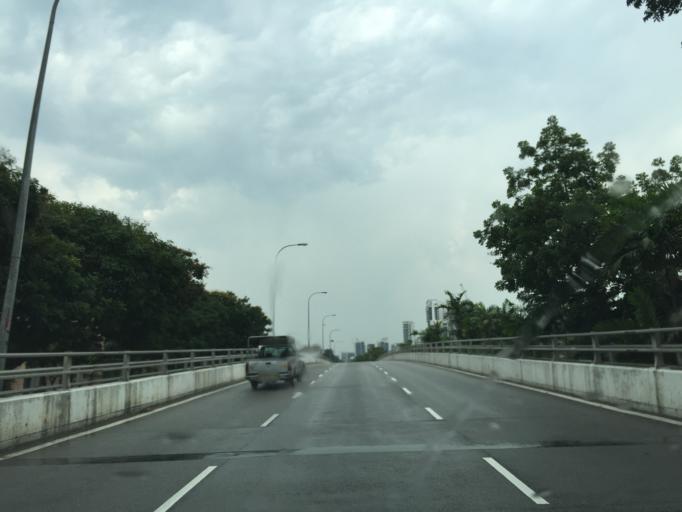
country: SG
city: Singapore
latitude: 1.3214
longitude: 103.8241
